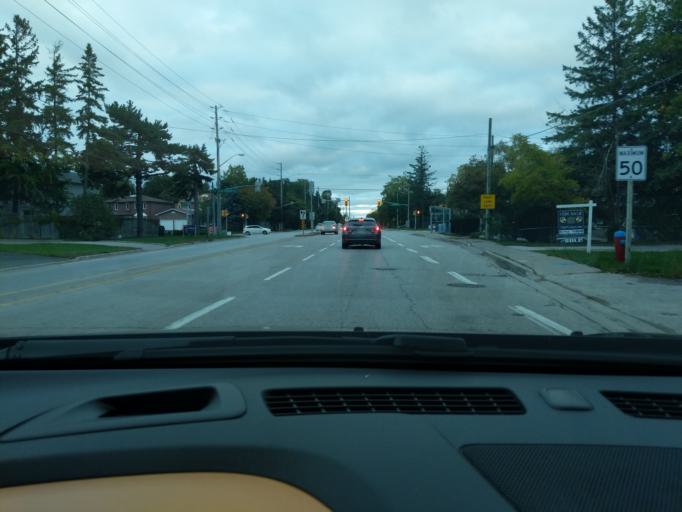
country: CA
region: Ontario
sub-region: York
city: Richmond Hill
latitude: 43.8871
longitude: -79.4533
